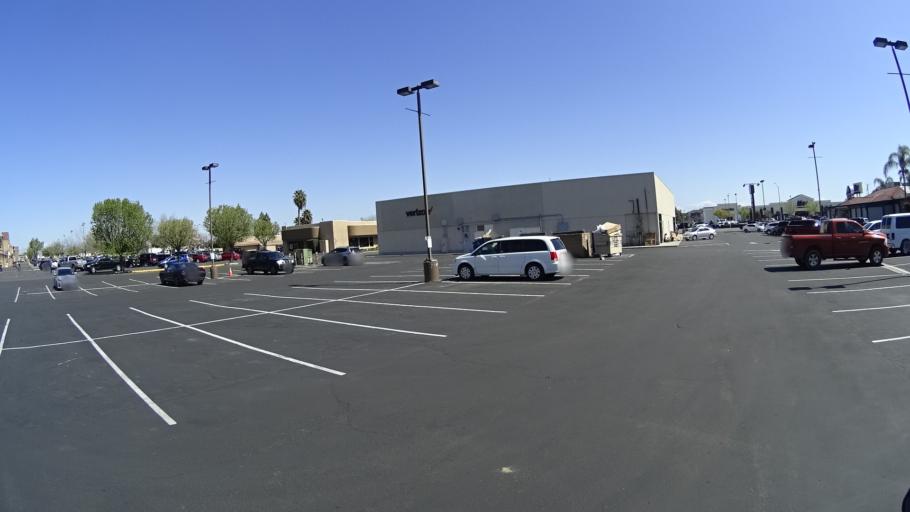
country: US
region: California
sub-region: Fresno County
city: Fresno
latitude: 36.8117
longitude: -119.7918
